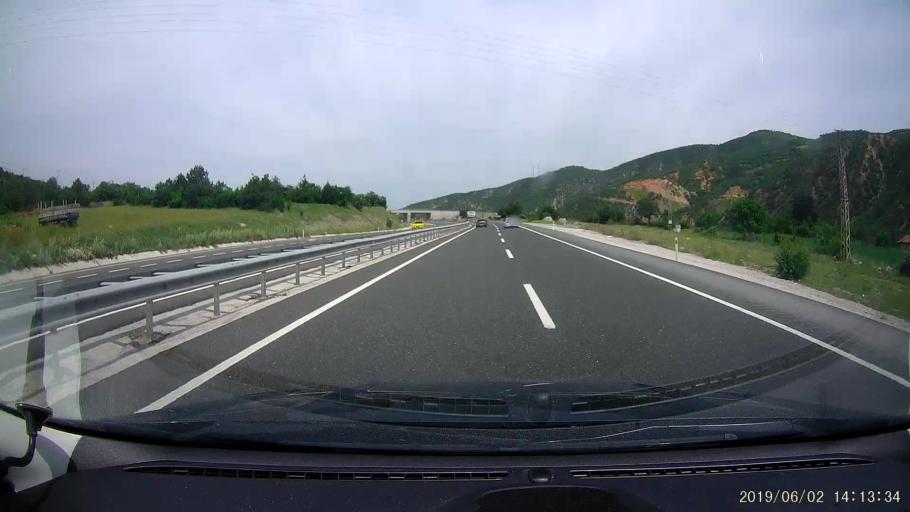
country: TR
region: Cankiri
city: Yaprakli
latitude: 40.9267
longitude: 33.8336
